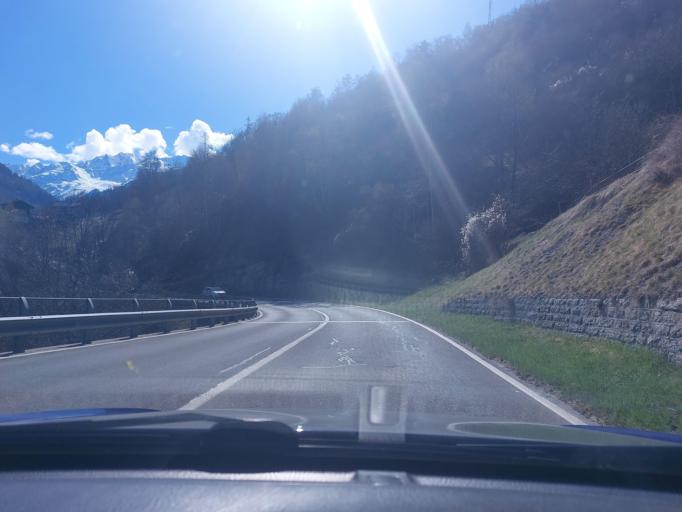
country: CH
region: Valais
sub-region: Herens District
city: Heremence
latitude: 46.1788
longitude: 7.4118
